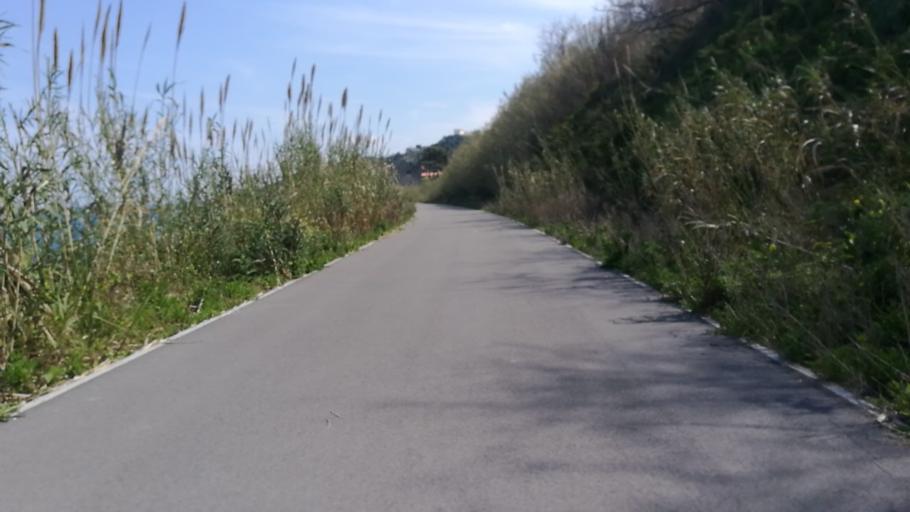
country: IT
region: Abruzzo
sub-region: Provincia di Chieti
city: Marina di San Vito
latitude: 42.3155
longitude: 14.4373
